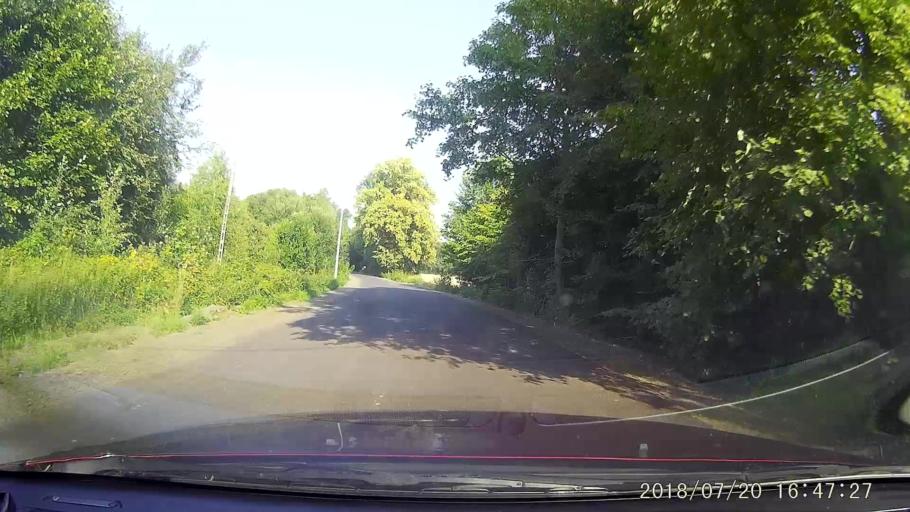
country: PL
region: Lower Silesian Voivodeship
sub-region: Powiat lubanski
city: Siekierczyn
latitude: 51.0597
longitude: 15.1783
